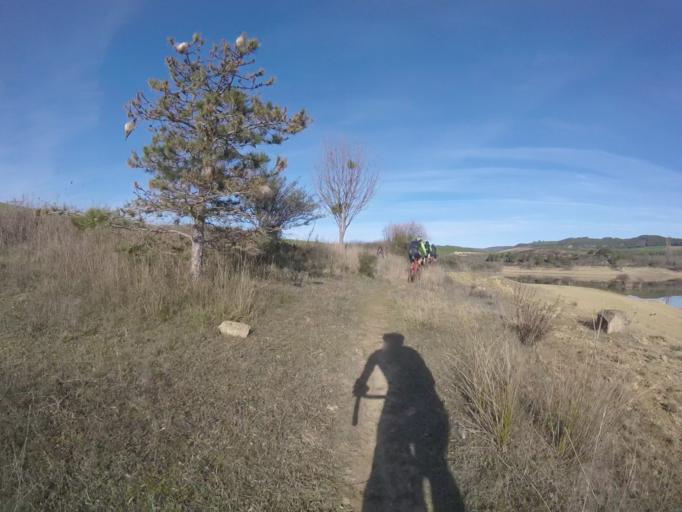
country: ES
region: Navarre
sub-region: Provincia de Navarra
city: Yerri
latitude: 42.7123
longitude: -1.9566
